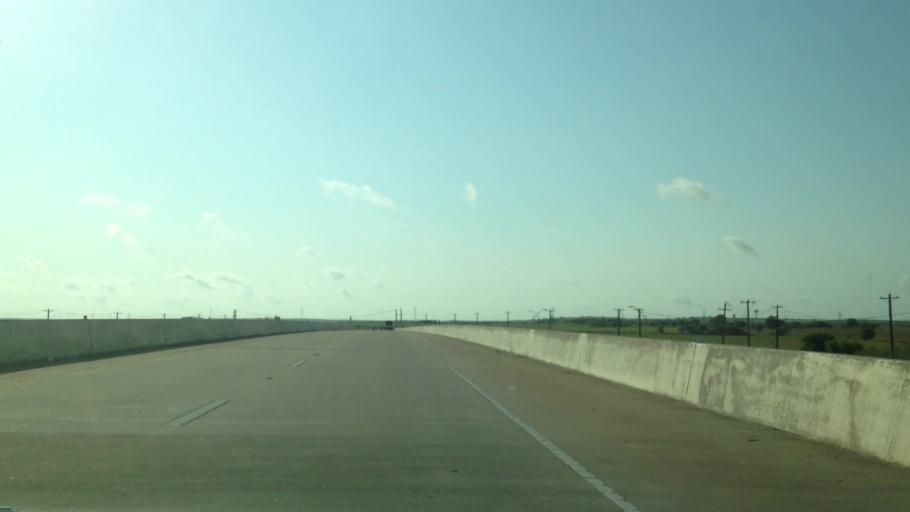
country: US
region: Texas
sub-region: Travis County
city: Onion Creek
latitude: 30.0841
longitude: -97.7369
